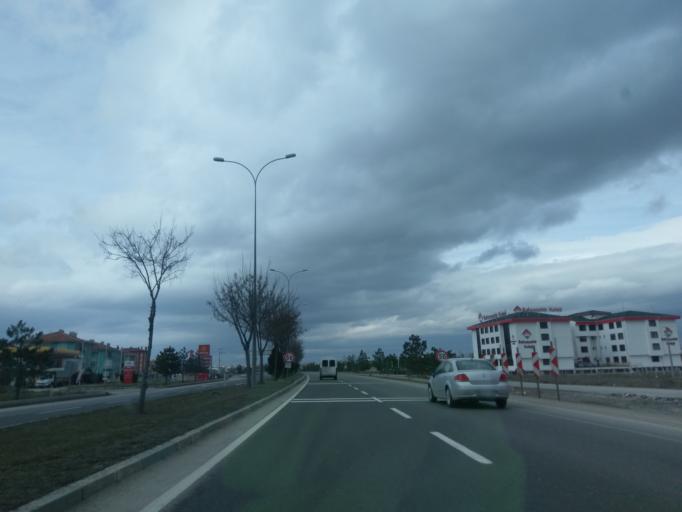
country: TR
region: Kuetahya
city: Kutahya
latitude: 39.4084
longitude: 30.0246
